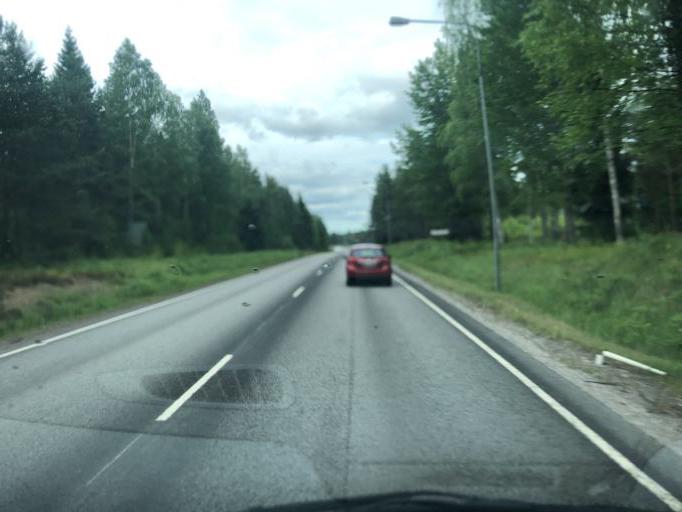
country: FI
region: Kymenlaakso
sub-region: Kouvola
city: Kouvola
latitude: 60.9164
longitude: 26.7776
